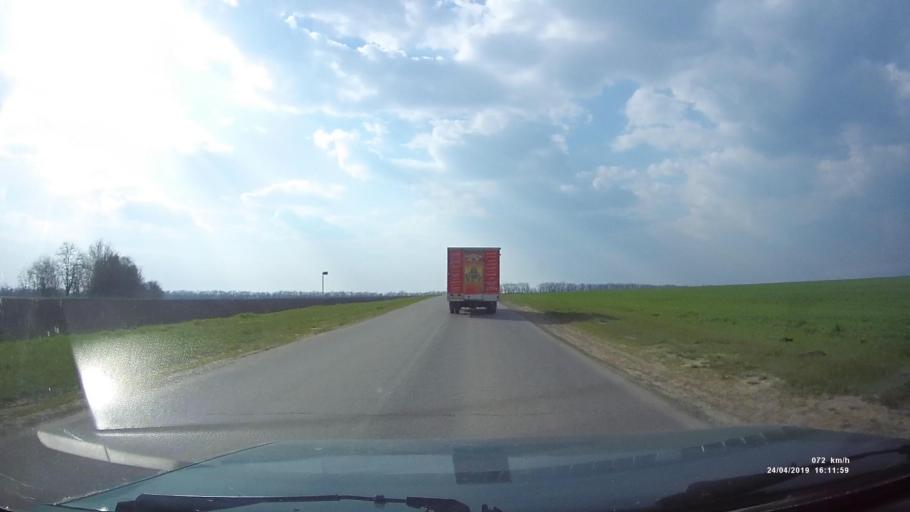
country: RU
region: Rostov
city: Sovetskoye
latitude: 46.7296
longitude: 42.2441
